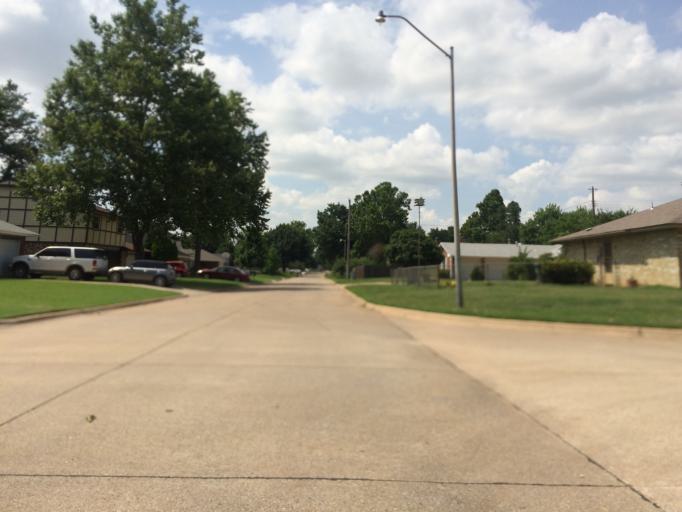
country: US
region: Oklahoma
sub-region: Cleveland County
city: Norman
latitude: 35.2114
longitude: -97.4821
